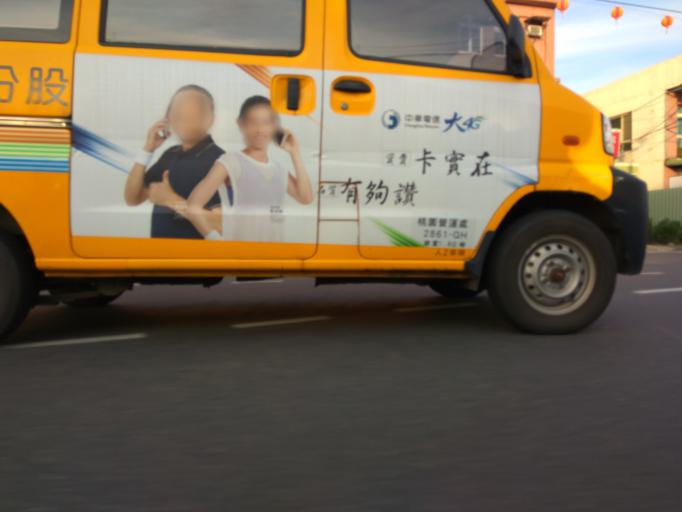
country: TW
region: Taiwan
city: Taoyuan City
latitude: 25.0099
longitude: 121.1409
